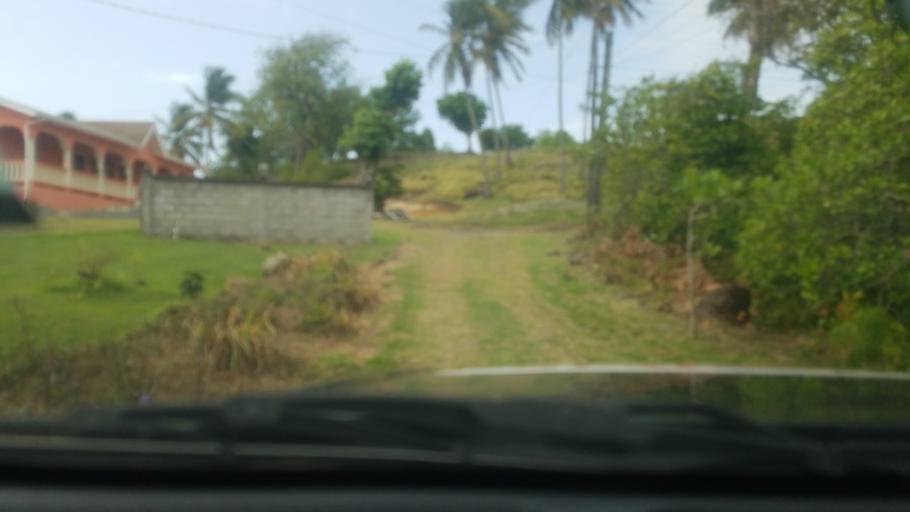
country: LC
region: Micoud Quarter
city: Micoud
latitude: 13.7991
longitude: -60.9143
